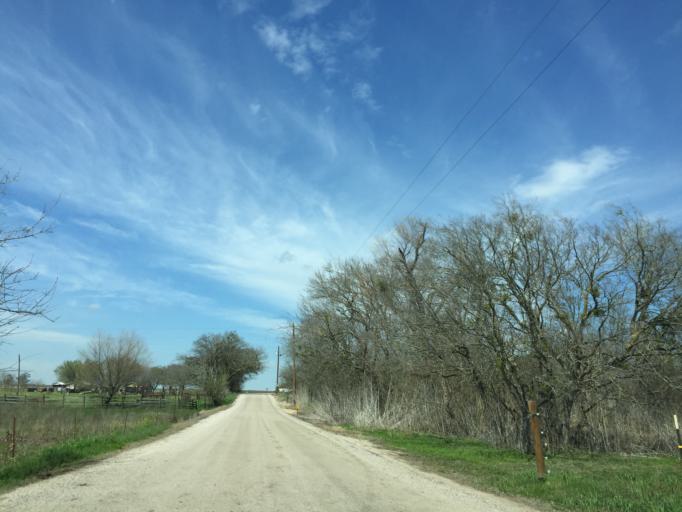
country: US
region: Texas
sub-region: Williamson County
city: Taylor
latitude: 30.5650
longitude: -97.3489
